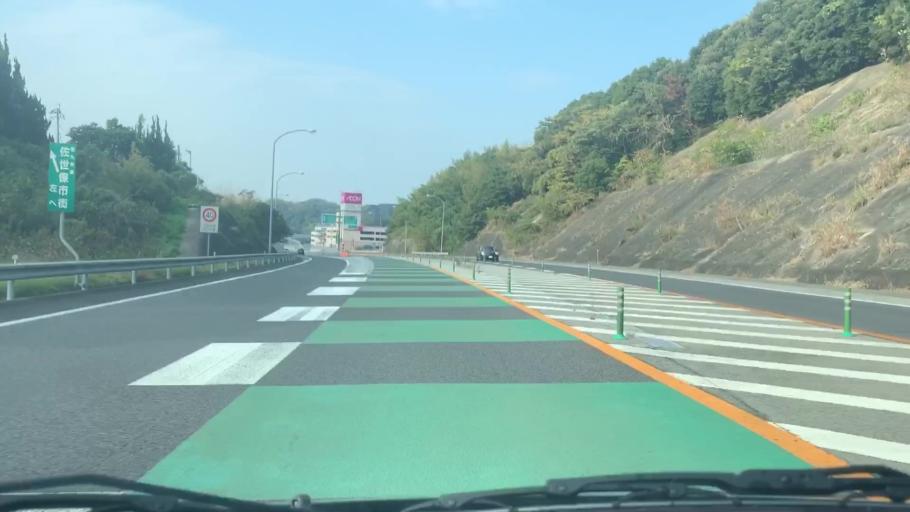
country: JP
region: Nagasaki
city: Sasebo
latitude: 33.1500
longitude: 129.7853
